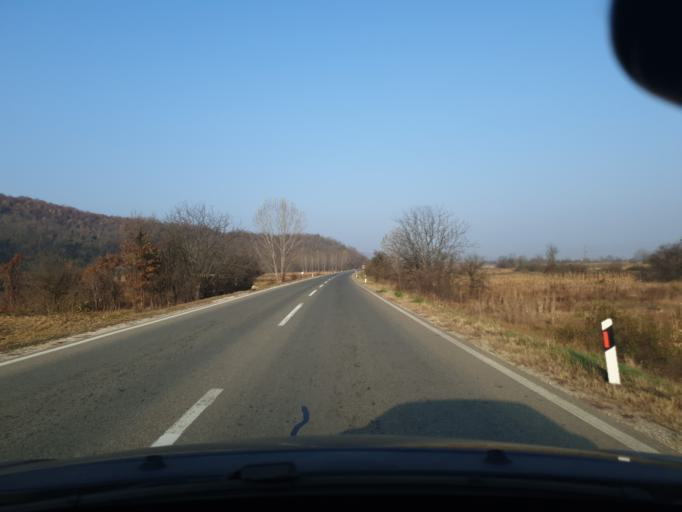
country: RS
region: Central Serbia
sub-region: Jablanicki Okrug
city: Vlasotince
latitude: 42.9163
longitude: 22.0310
